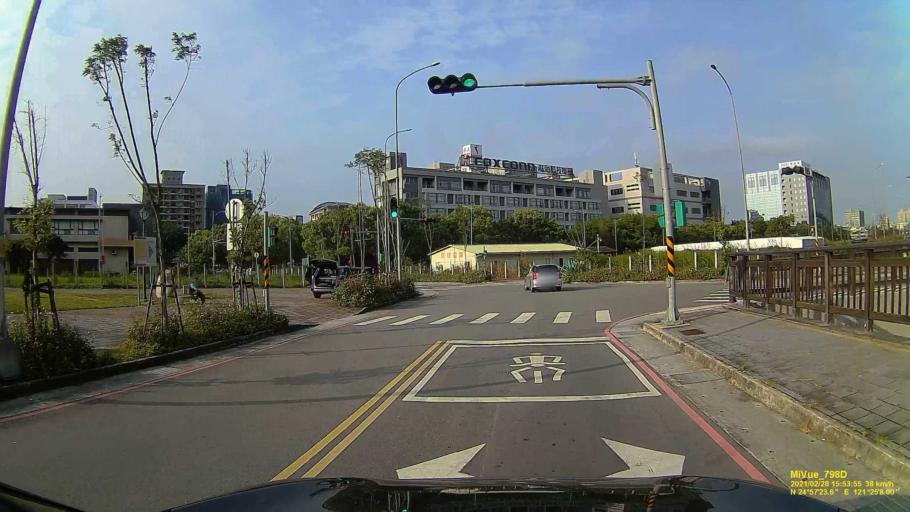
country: TW
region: Taipei
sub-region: Taipei
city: Banqiao
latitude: 24.9568
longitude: 121.4189
